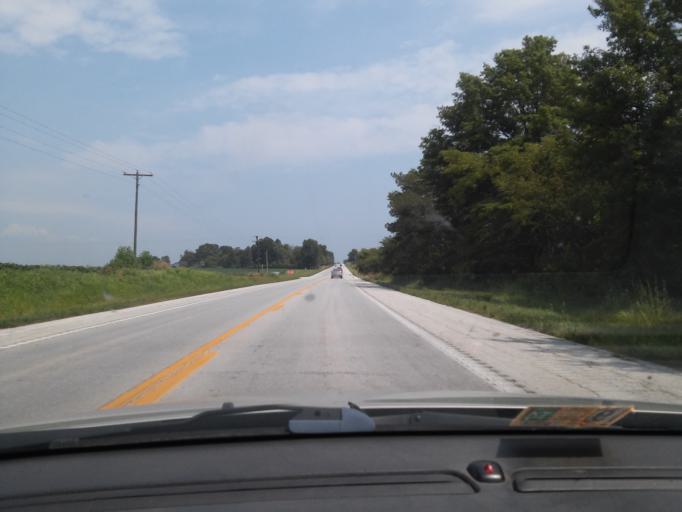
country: US
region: Missouri
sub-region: Montgomery County
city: Wellsville
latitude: 39.2061
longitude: -91.6466
